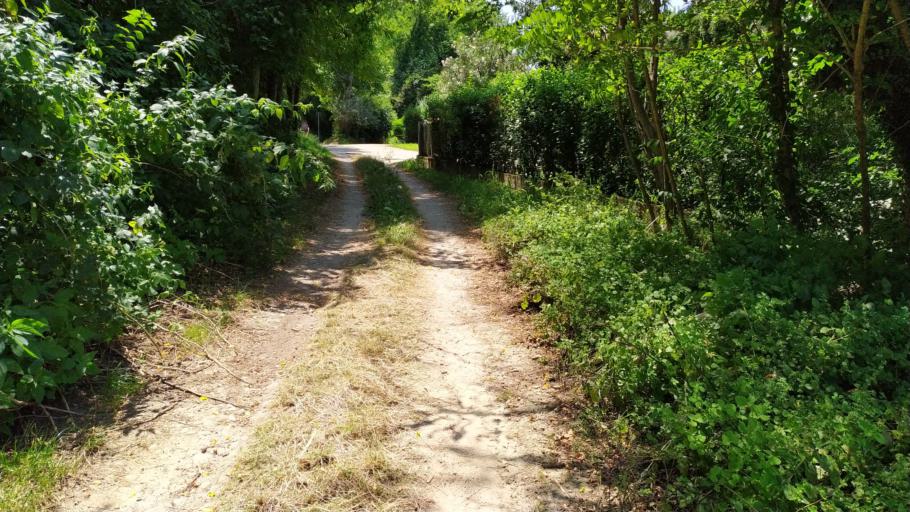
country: IT
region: Emilia-Romagna
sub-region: Forli-Cesena
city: Castrocaro Terme e Terra del Sole
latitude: 44.1884
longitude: 11.9661
